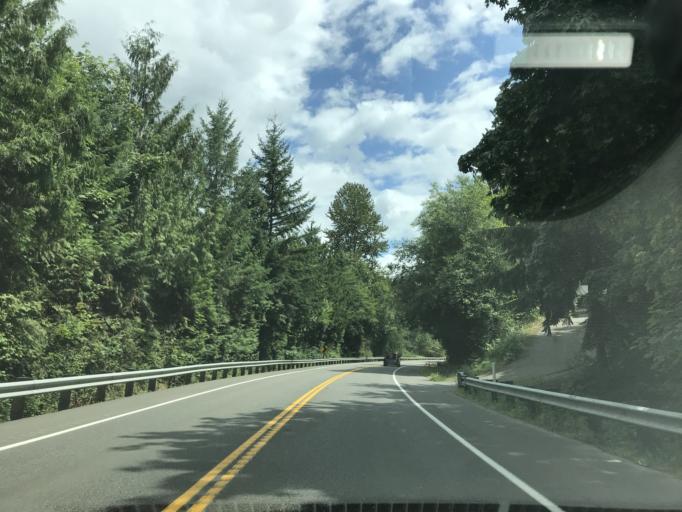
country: US
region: Washington
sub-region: King County
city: Maple Heights-Lake Desire
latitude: 47.4211
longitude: -122.0758
